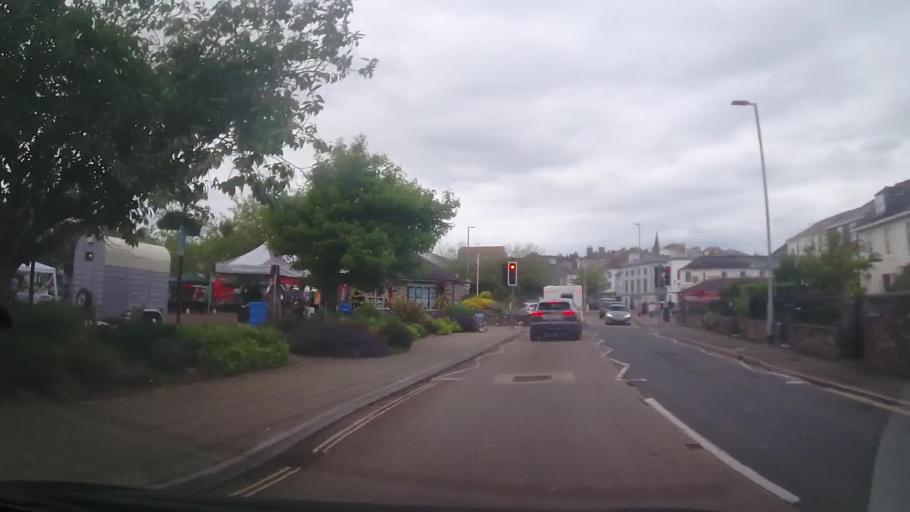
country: GB
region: England
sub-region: Devon
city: Kingsbridge
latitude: 50.2828
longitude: -3.7762
